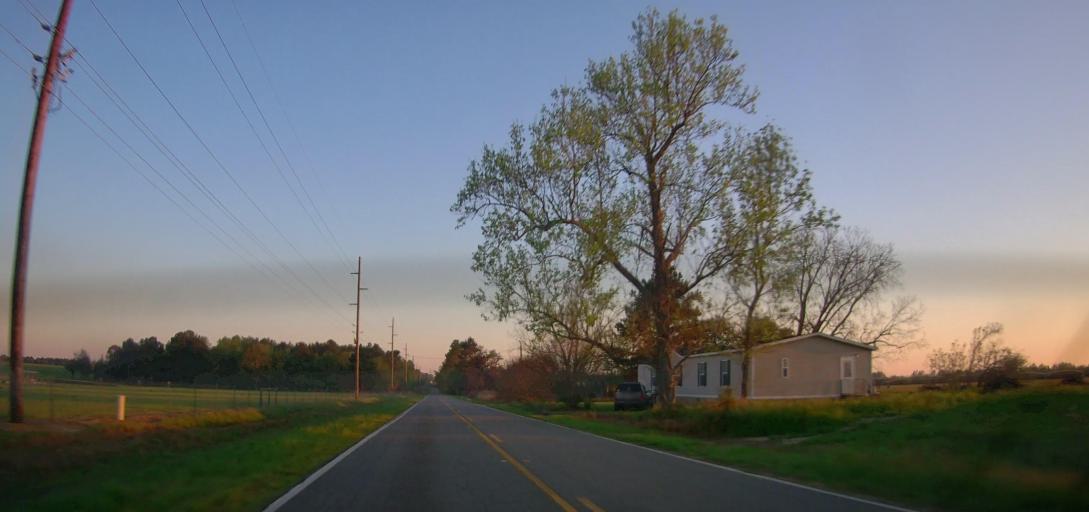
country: US
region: Georgia
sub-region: Ben Hill County
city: Fitzgerald
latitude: 31.7662
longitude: -83.3548
